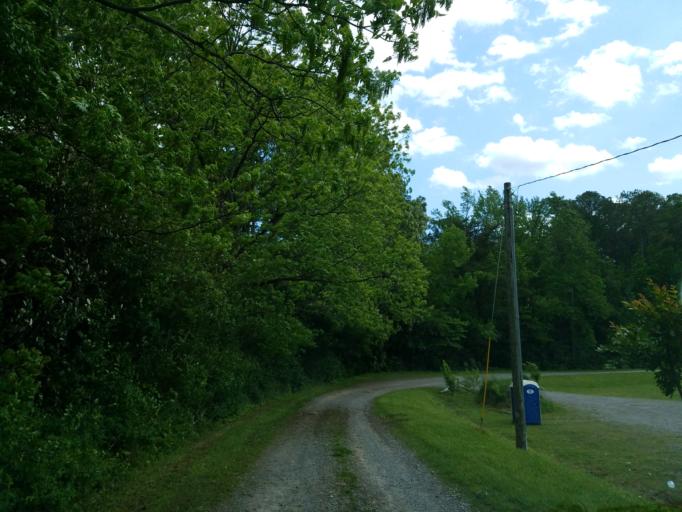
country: US
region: Georgia
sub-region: Pickens County
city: Jasper
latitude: 34.4659
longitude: -84.4317
